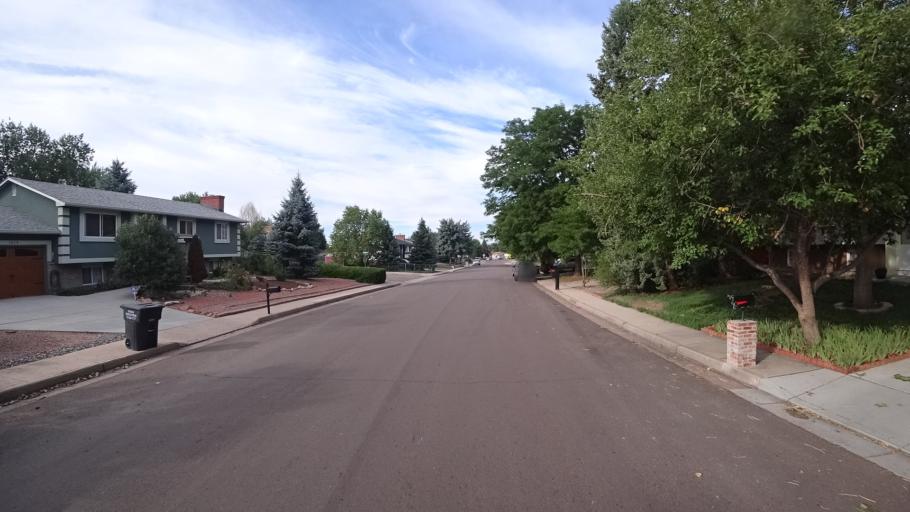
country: US
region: Colorado
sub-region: El Paso County
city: Security-Widefield
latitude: 38.7292
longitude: -104.6925
